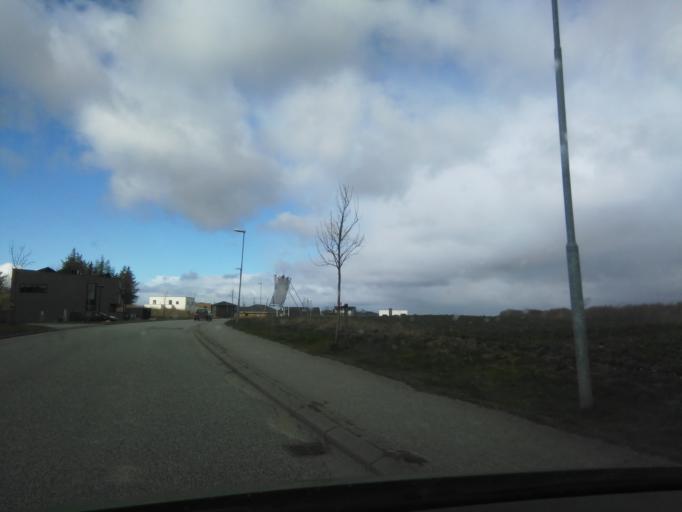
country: DK
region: Central Jutland
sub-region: Arhus Kommune
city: Marslet
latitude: 56.0582
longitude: 10.1667
